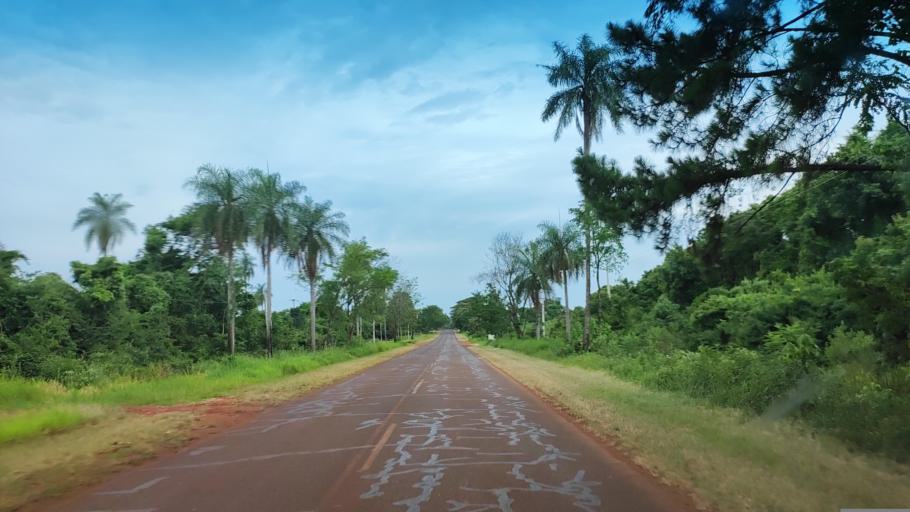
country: AR
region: Misiones
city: Gobernador Roca
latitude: -27.1450
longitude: -55.4936
